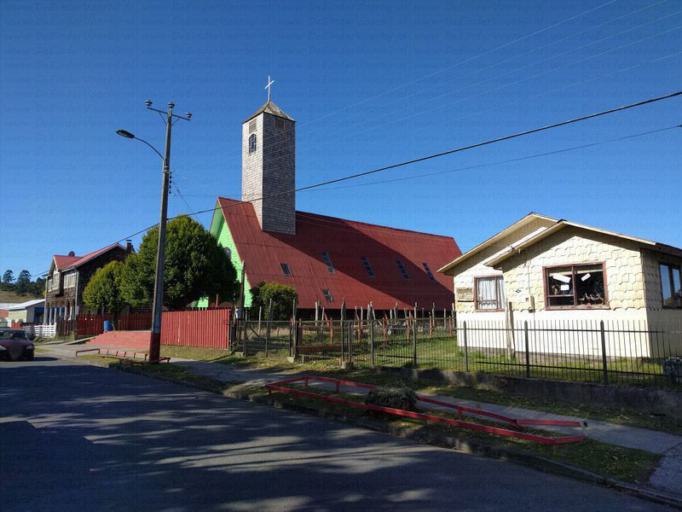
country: CL
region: Los Lagos
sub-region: Provincia de Chiloe
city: Castro
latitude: -42.4398
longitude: -73.6023
